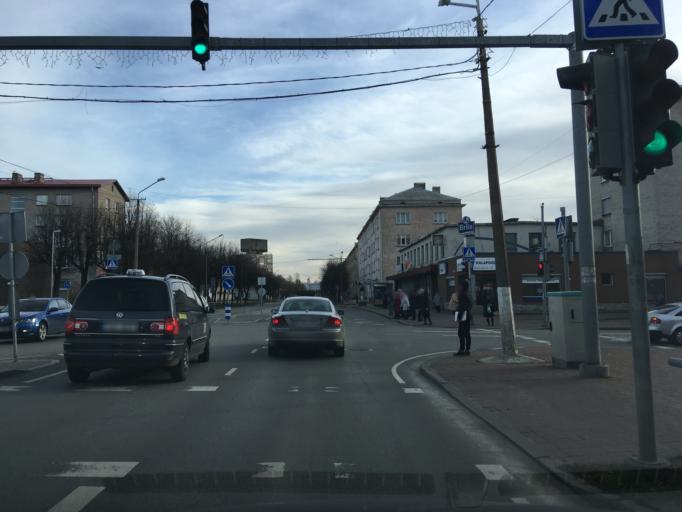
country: EE
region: Ida-Virumaa
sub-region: Narva linn
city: Narva
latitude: 59.3781
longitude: 28.1856
